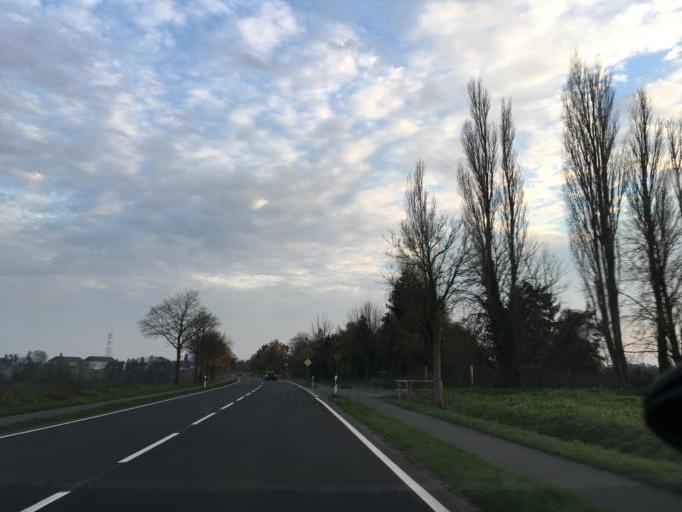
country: DE
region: Lower Saxony
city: Celle
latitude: 52.6457
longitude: 10.0741
